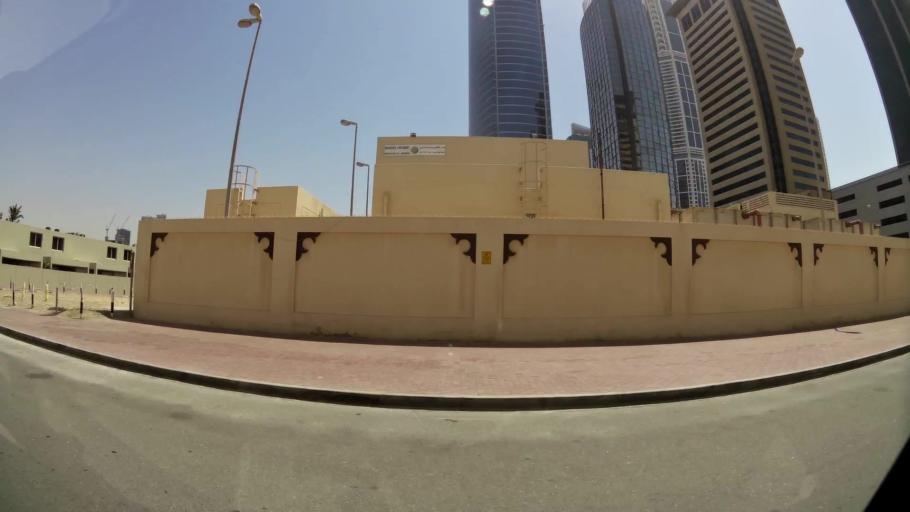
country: AE
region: Dubai
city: Dubai
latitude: 25.0906
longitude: 55.1545
